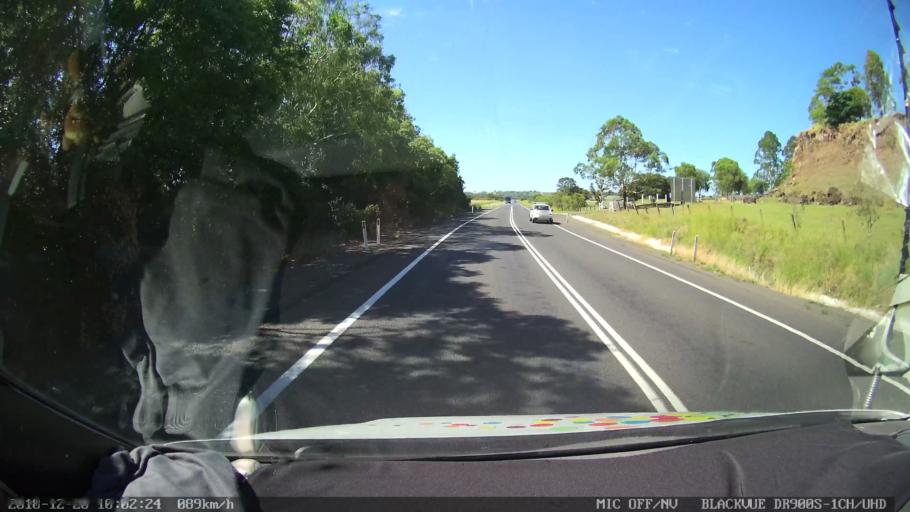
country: AU
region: New South Wales
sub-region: Lismore Municipality
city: East Lismore
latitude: -28.8575
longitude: 153.2613
